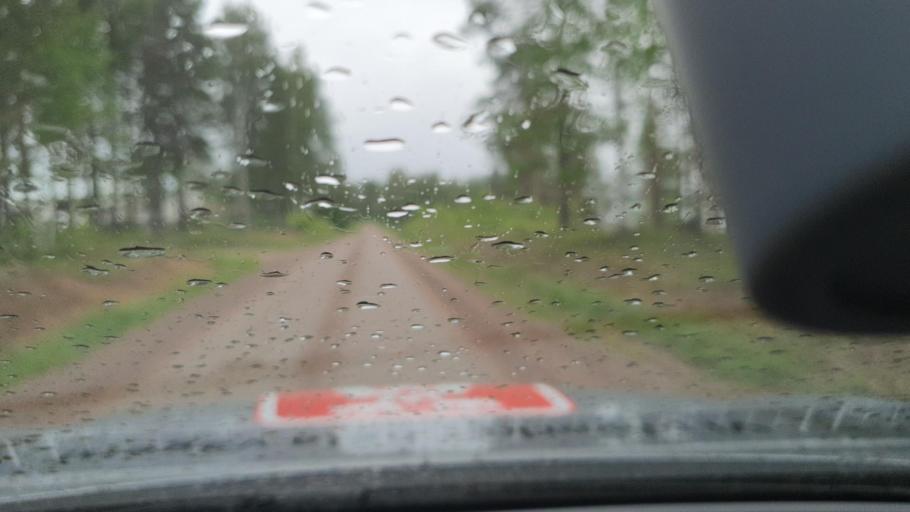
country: SE
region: Norrbotten
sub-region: Overkalix Kommun
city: OEverkalix
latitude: 66.5002
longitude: 22.7594
